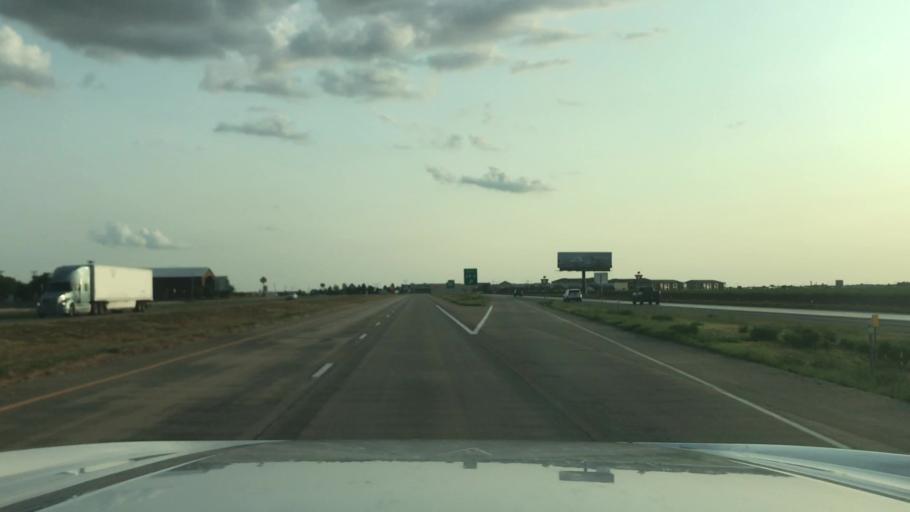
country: US
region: Texas
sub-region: Hale County
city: Plainview
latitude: 34.2019
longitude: -101.7450
